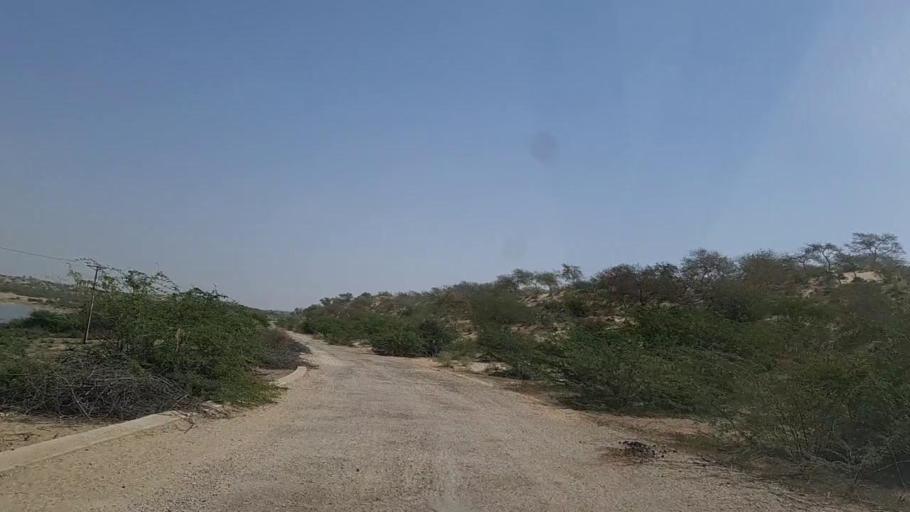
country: PK
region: Sindh
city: Diplo
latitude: 24.5136
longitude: 69.3687
